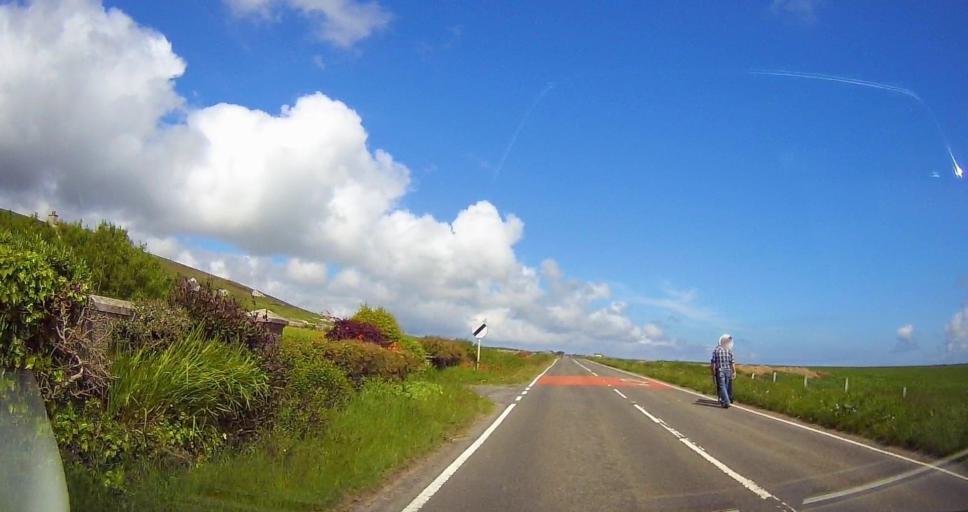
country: GB
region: Scotland
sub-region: Orkney Islands
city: Orkney
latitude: 59.0133
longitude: -3.1097
